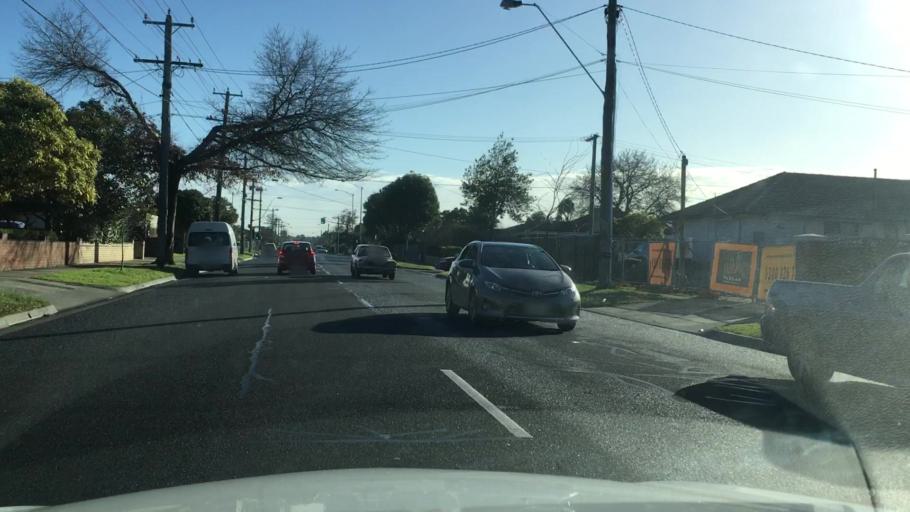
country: AU
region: Victoria
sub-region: Greater Dandenong
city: Noble Park
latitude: -37.9693
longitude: 145.1675
